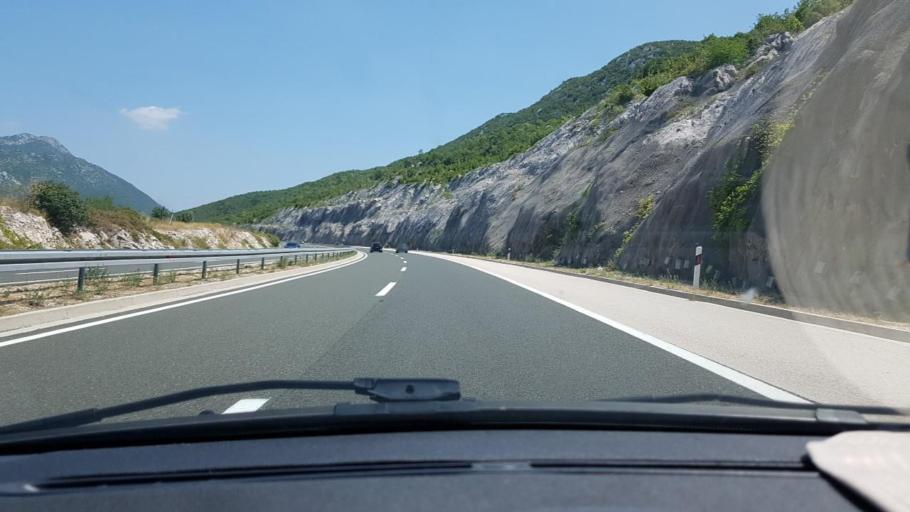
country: HR
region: Splitsko-Dalmatinska
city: Vrgorac
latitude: 43.2257
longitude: 17.2379
